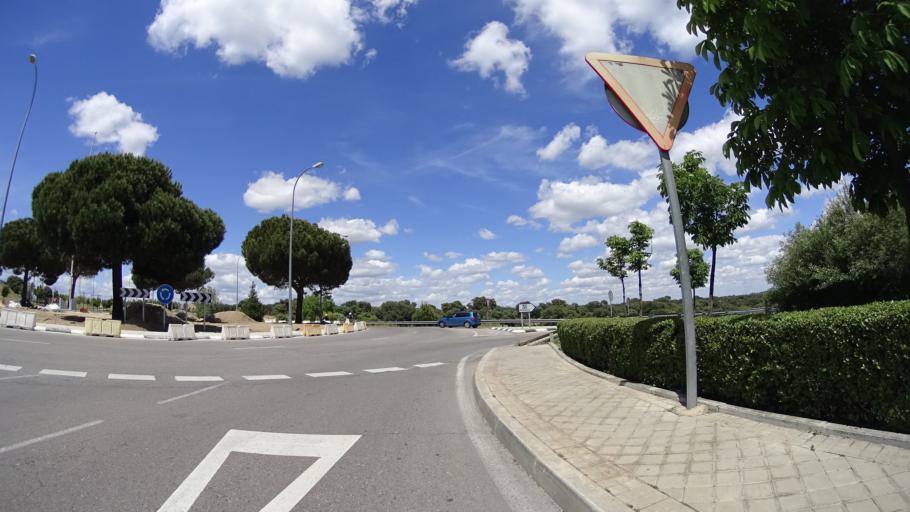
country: ES
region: Madrid
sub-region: Provincia de Madrid
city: Boadilla del Monte
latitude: 40.4108
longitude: -3.8809
